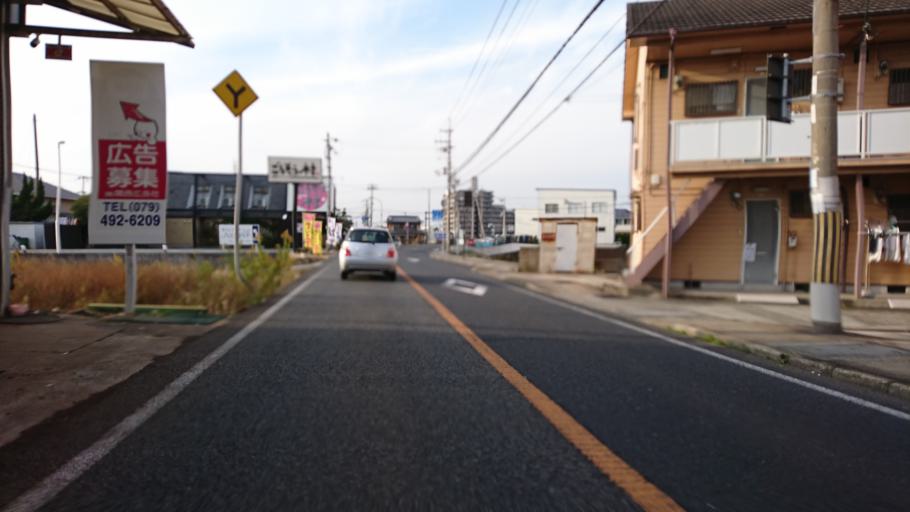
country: JP
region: Hyogo
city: Kakogawacho-honmachi
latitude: 34.7116
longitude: 134.8638
